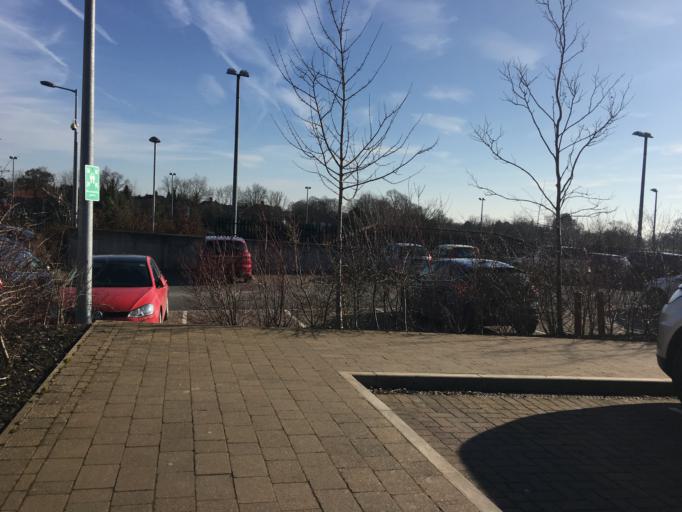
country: GB
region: England
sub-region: Warwickshire
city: Rugby
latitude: 52.3663
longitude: -1.2538
